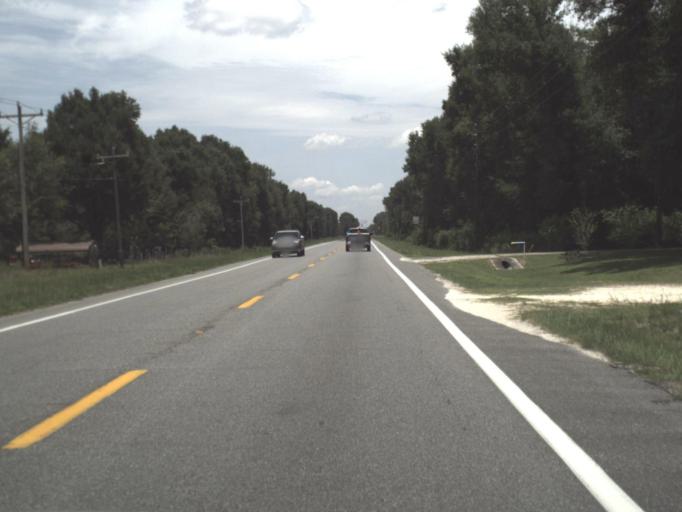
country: US
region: Florida
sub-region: Lafayette County
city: Mayo
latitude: 30.0879
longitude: -83.1727
